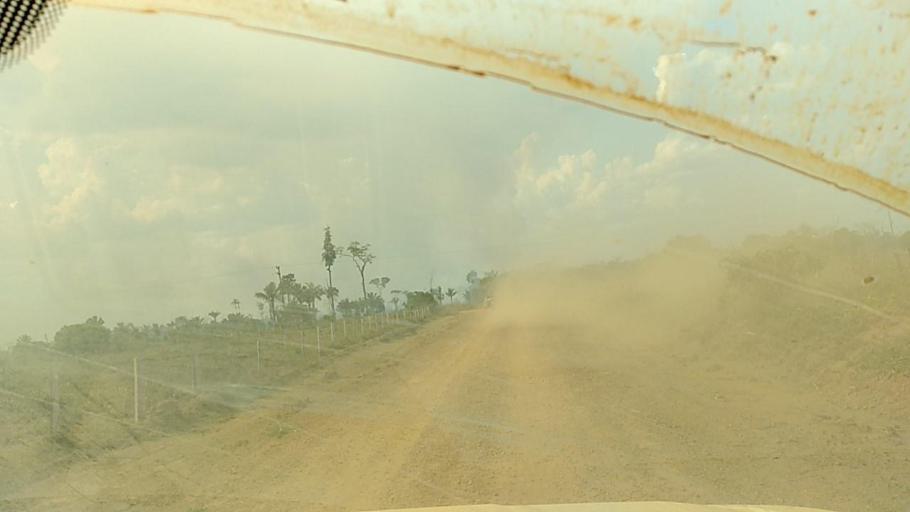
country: BR
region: Rondonia
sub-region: Porto Velho
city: Porto Velho
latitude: -8.6845
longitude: -63.2392
